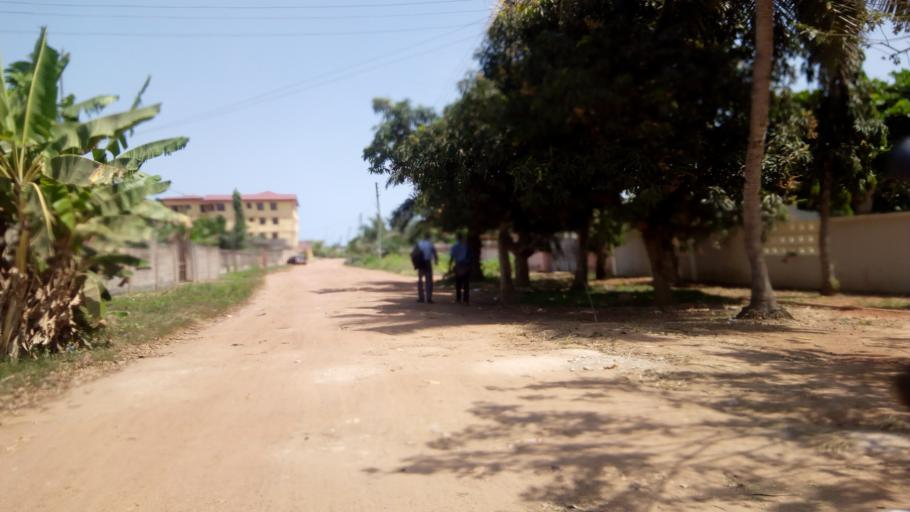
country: GH
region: Central
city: Cape Coast
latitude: 5.1336
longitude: -1.2831
